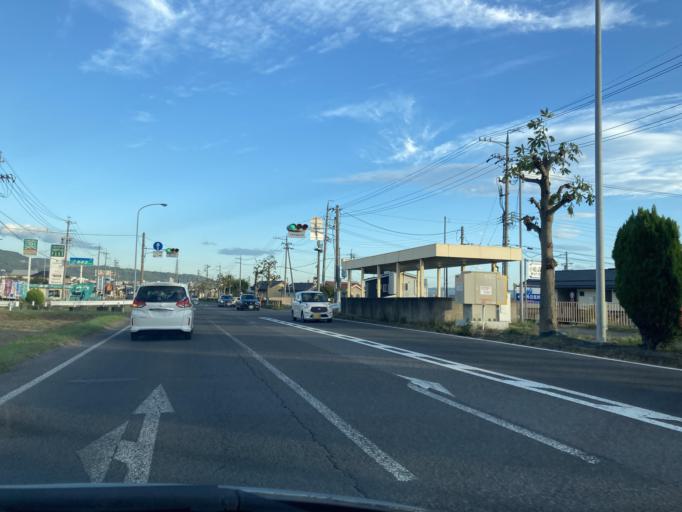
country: JP
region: Nagano
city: Ueda
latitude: 36.4111
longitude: 138.2632
